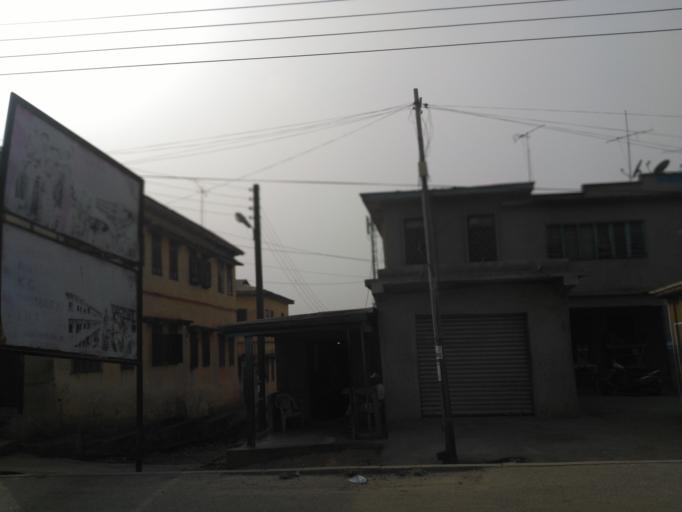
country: GH
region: Ashanti
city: Kumasi
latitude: 6.6993
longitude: -1.6106
